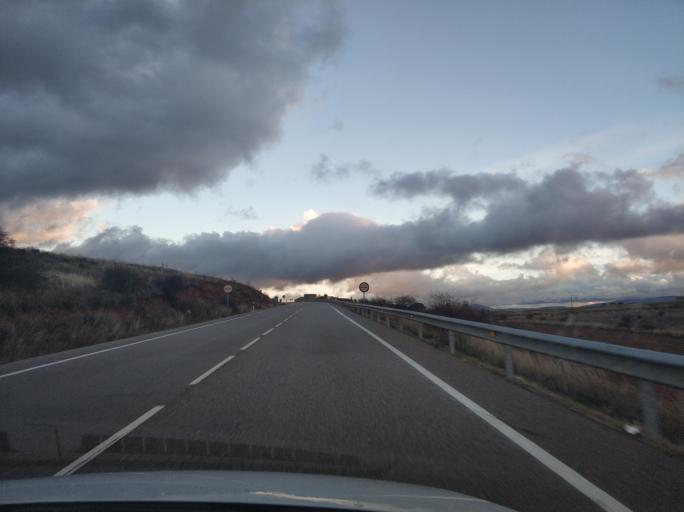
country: ES
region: Castille and Leon
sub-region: Provincia de Segovia
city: Ayllon
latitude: 41.4149
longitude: -3.4014
